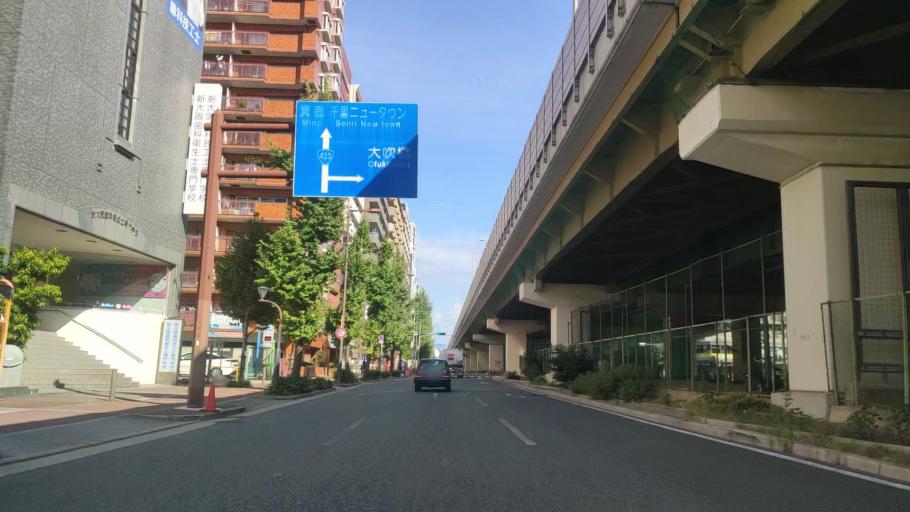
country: JP
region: Osaka
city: Suita
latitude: 34.7435
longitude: 135.4980
